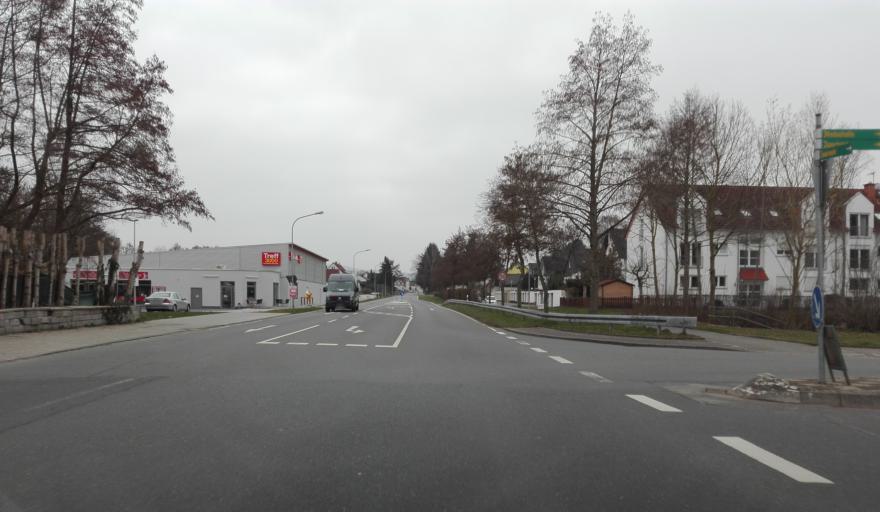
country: DE
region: Hesse
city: Ober-Ramstadt
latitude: 49.7948
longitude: 8.7389
